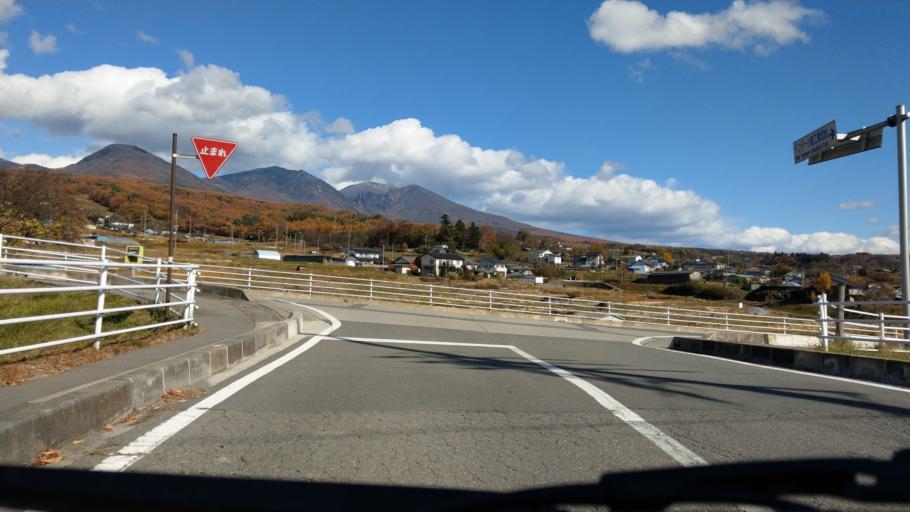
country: JP
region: Nagano
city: Komoro
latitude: 36.3493
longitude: 138.4051
